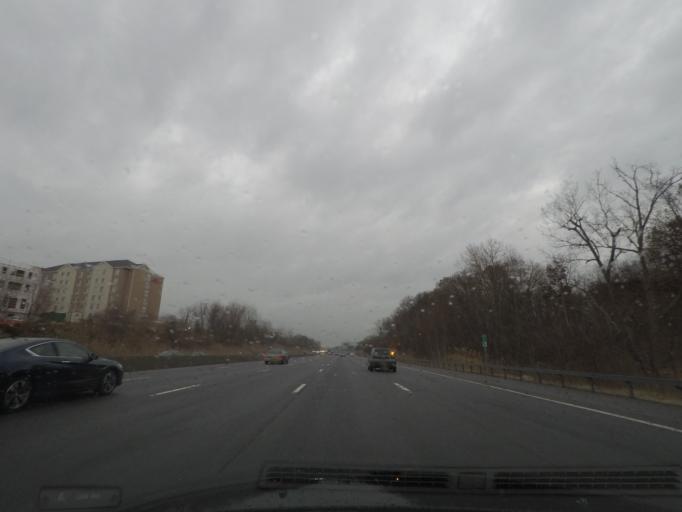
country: US
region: New York
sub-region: Albany County
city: Roessleville
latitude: 42.6888
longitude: -73.8138
